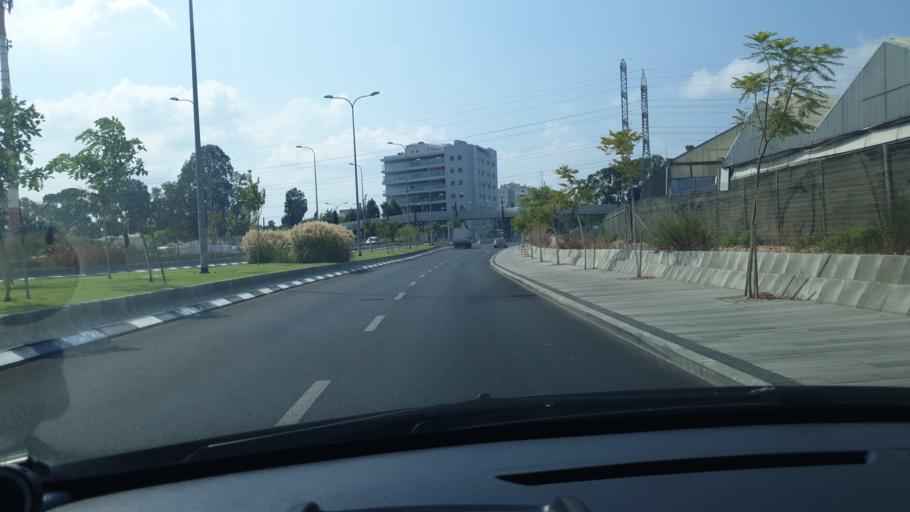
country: IL
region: Haifa
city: Qiryat Bialik
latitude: 32.8156
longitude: 35.0822
